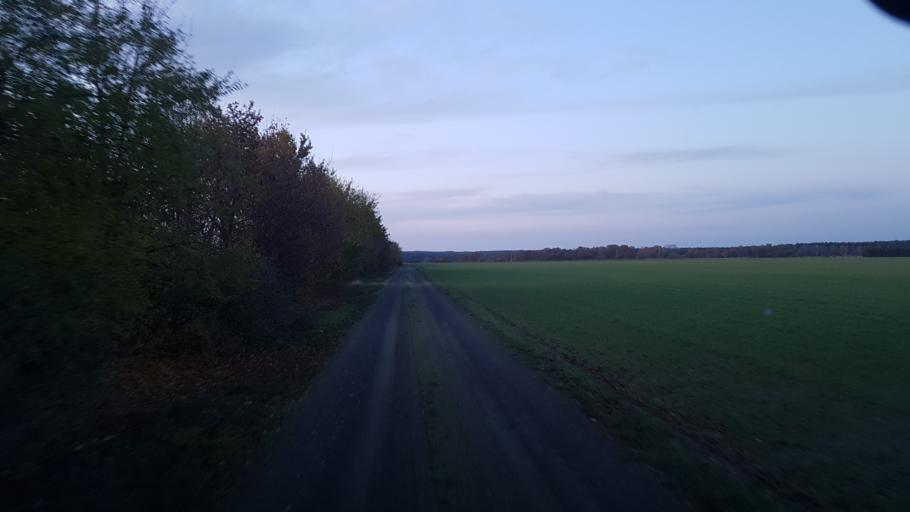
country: DE
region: Brandenburg
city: Schilda
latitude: 51.6290
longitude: 13.3293
